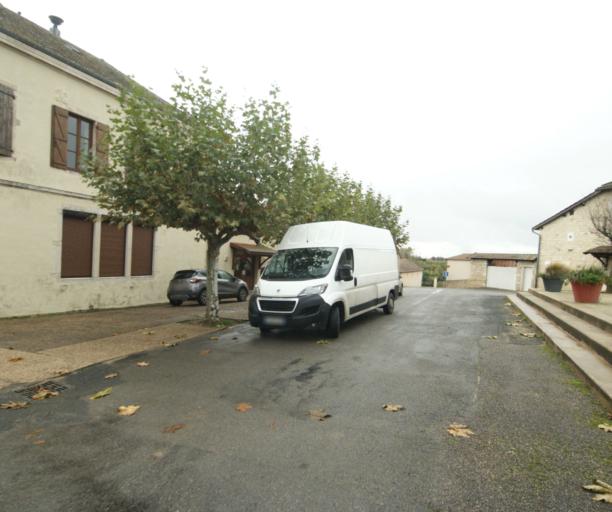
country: FR
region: Rhone-Alpes
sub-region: Departement de l'Ain
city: Pont-de-Vaux
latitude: 46.4758
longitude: 4.8721
